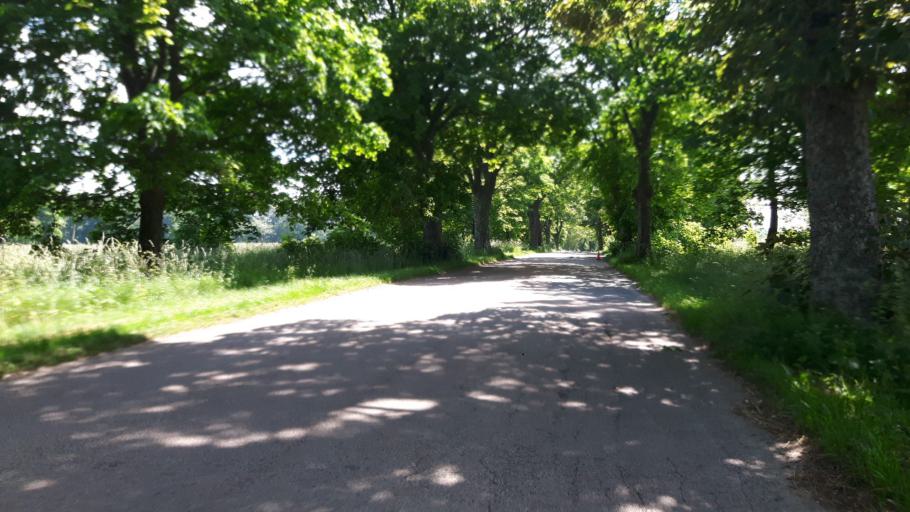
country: PL
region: Pomeranian Voivodeship
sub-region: Powiat wejherowski
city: Choczewo
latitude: 54.7430
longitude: 17.8116
